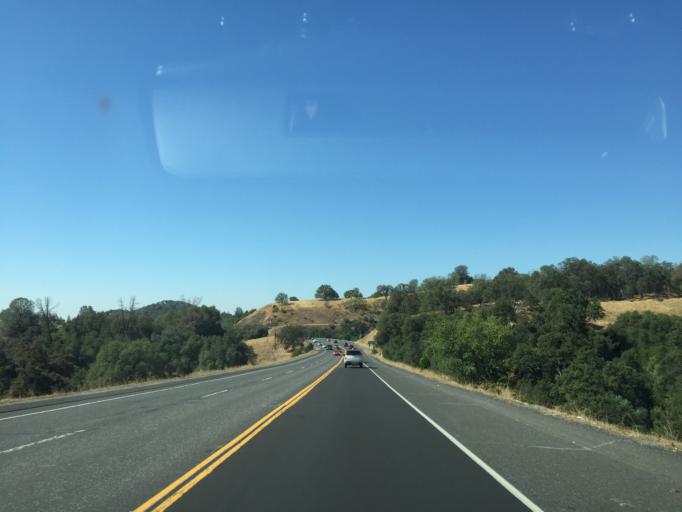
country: US
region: California
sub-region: Tuolumne County
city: East Sonora
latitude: 37.9697
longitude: -120.3724
